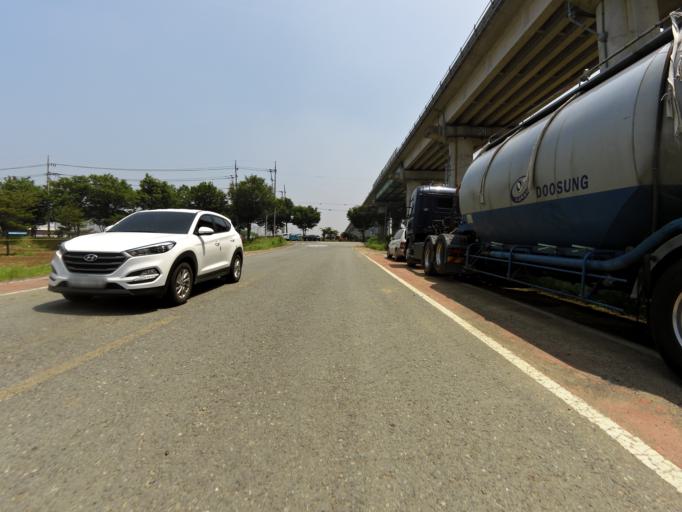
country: KR
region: Gyeongsangbuk-do
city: Gyeongsan-si
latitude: 35.8559
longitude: 128.7207
